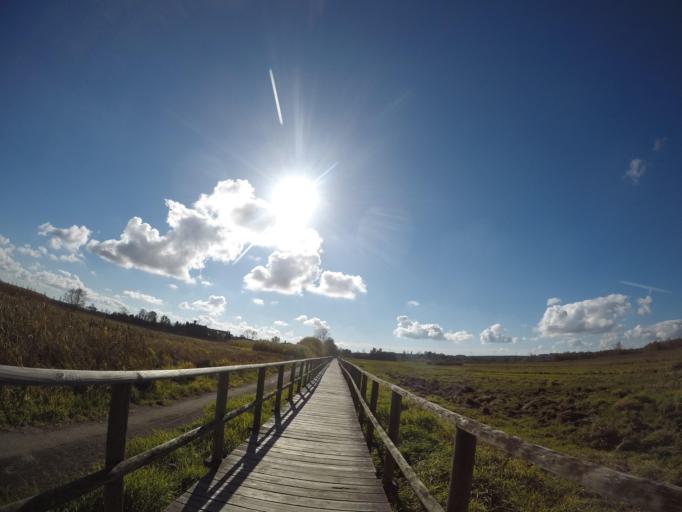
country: DE
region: Baden-Wuerttemberg
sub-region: Tuebingen Region
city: Bad Buchau
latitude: 48.0746
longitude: 9.6045
